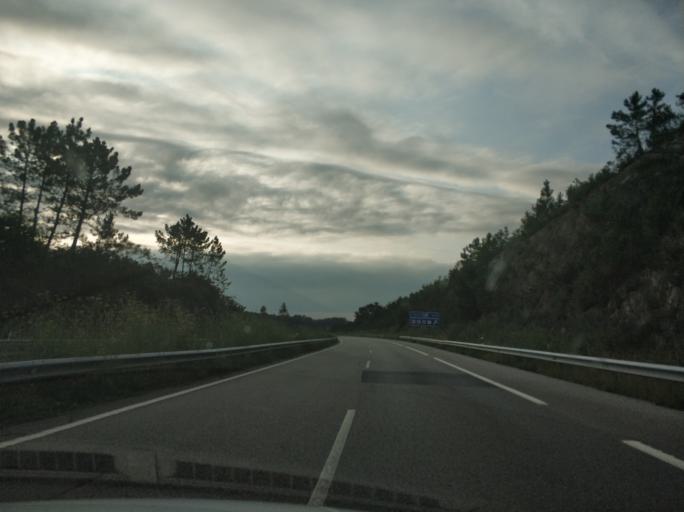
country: ES
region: Asturias
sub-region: Province of Asturias
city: Cudillero
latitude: 43.5659
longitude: -6.2155
